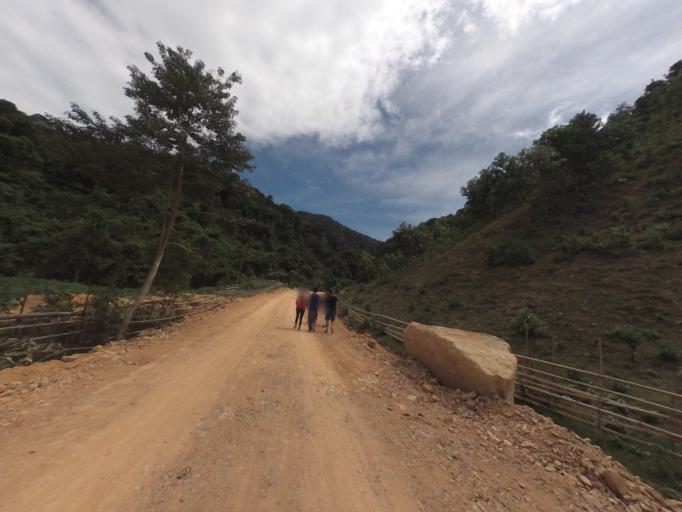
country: VN
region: Thua Thien-Hue
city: A Luoi
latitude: 16.3064
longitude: 107.2159
